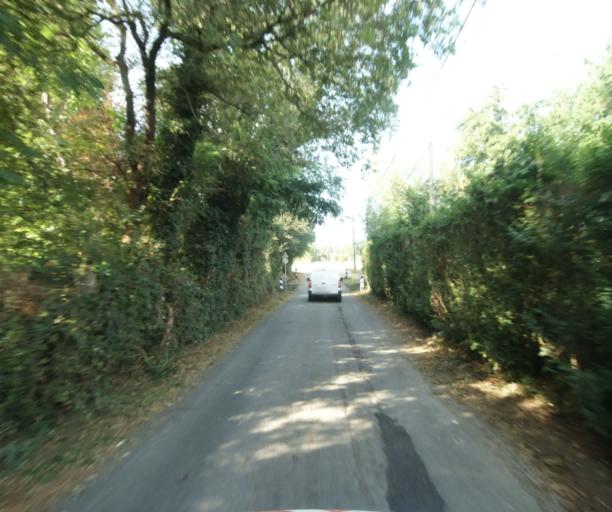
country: FR
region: Midi-Pyrenees
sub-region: Departement de la Haute-Garonne
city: Revel
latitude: 43.4715
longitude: 1.9974
